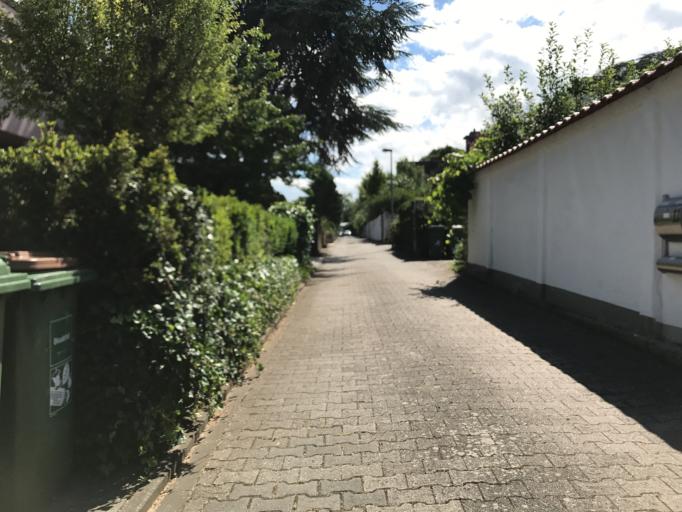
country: DE
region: Rheinland-Pfalz
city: Mainz
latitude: 49.9849
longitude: 8.2984
